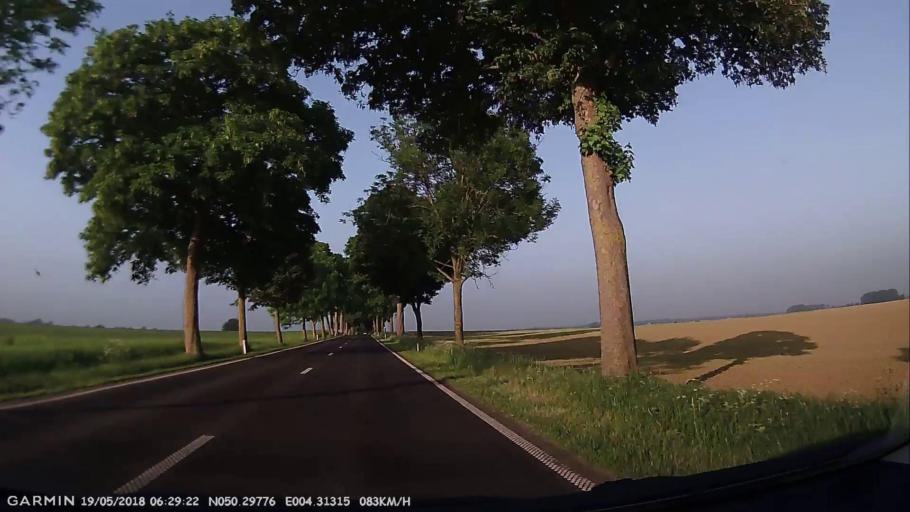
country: BE
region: Wallonia
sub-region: Province du Hainaut
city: Thuin
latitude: 50.2977
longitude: 4.3131
